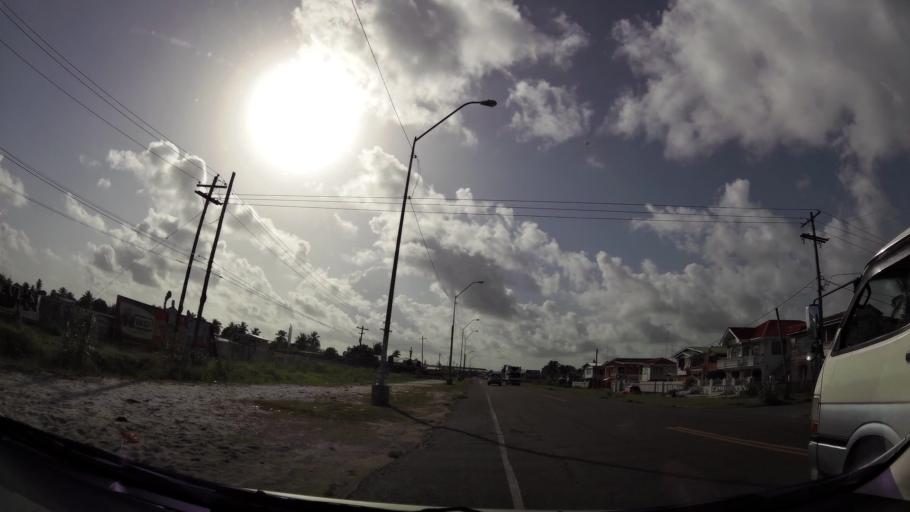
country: GY
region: Demerara-Mahaica
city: Georgetown
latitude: 6.8186
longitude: -58.0882
